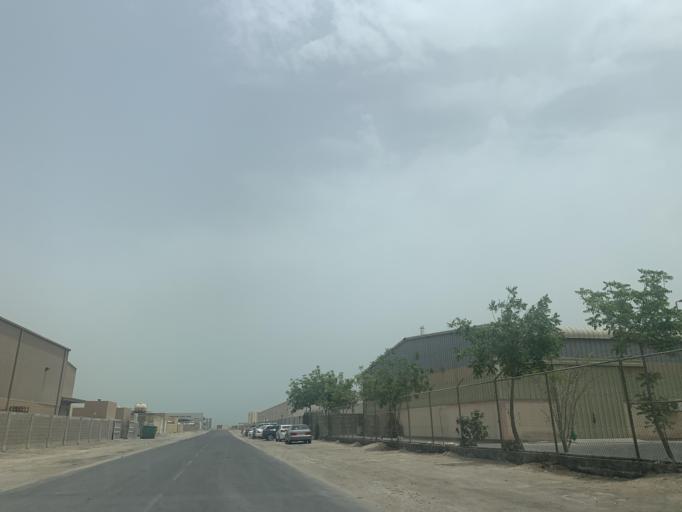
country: BH
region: Northern
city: Sitrah
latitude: 26.1774
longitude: 50.6223
